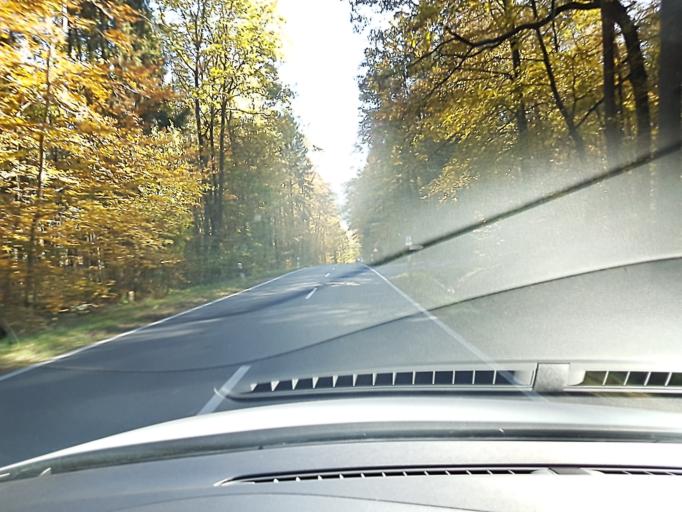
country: DE
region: Bavaria
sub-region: Regierungsbezirk Unterfranken
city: Leidersbach
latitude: 49.8780
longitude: 9.2390
